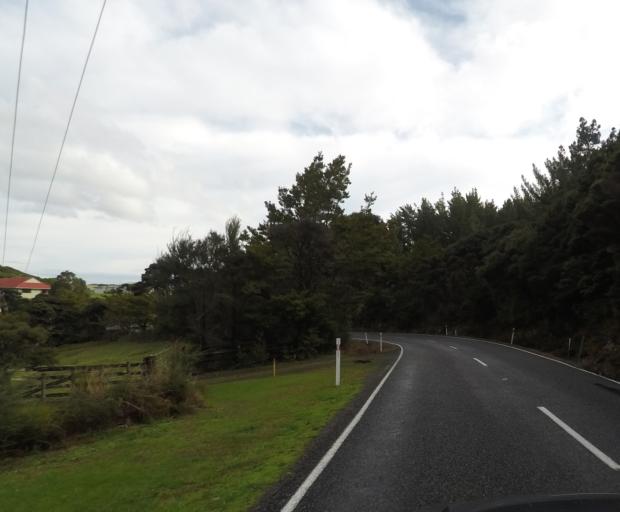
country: NZ
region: Northland
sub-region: Whangarei
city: Ruakaka
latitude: -36.0524
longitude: 174.5463
